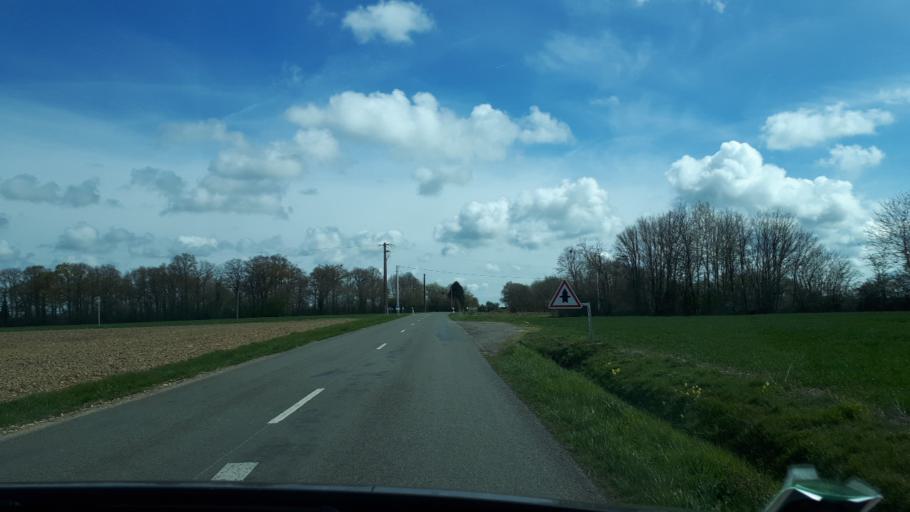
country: FR
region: Pays de la Loire
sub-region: Departement de la Sarthe
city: Bouloire
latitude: 47.8990
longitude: 0.5944
